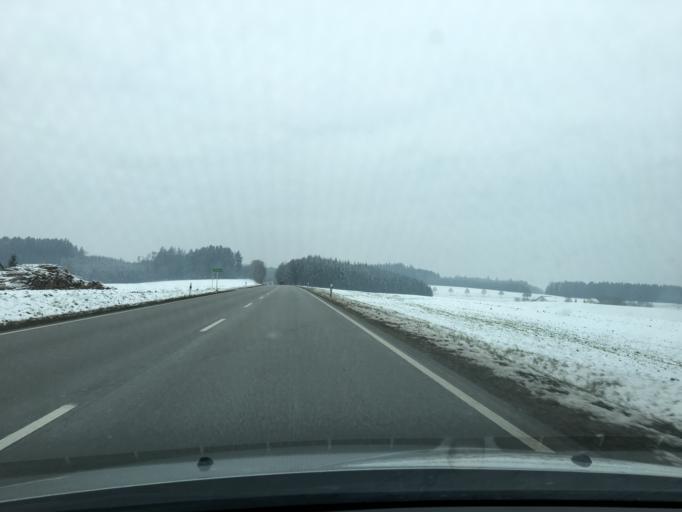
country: DE
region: Bavaria
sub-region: Lower Bavaria
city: Geisenhausen
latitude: 48.4962
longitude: 12.2253
